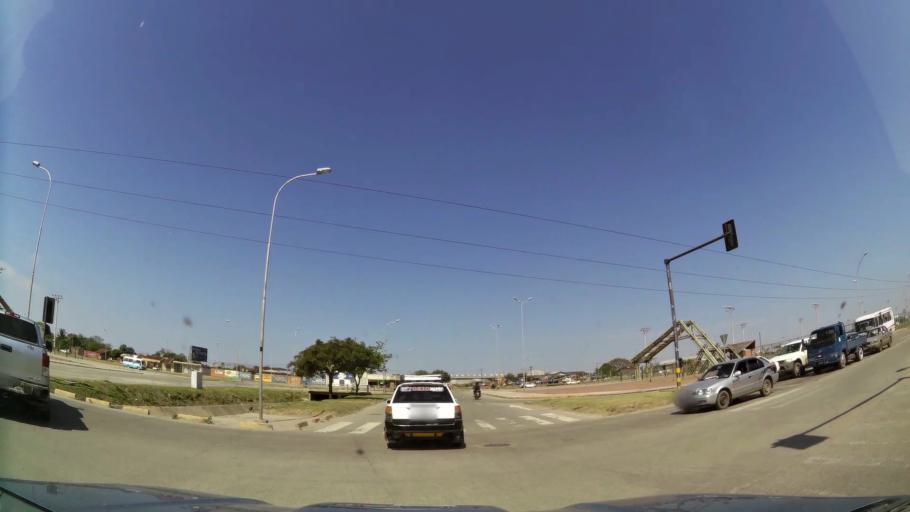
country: BO
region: Santa Cruz
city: Santa Cruz de la Sierra
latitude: -17.7363
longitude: -63.1426
